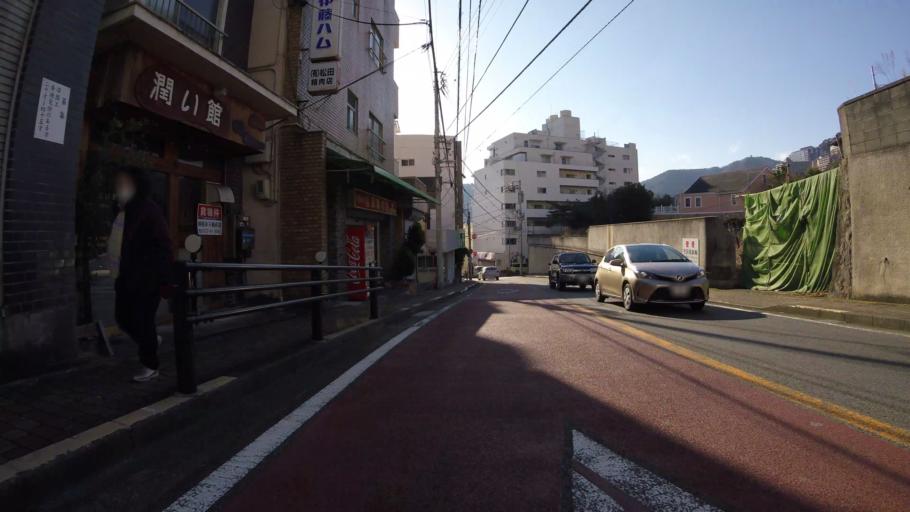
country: JP
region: Shizuoka
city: Atami
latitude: 35.0984
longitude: 139.0676
